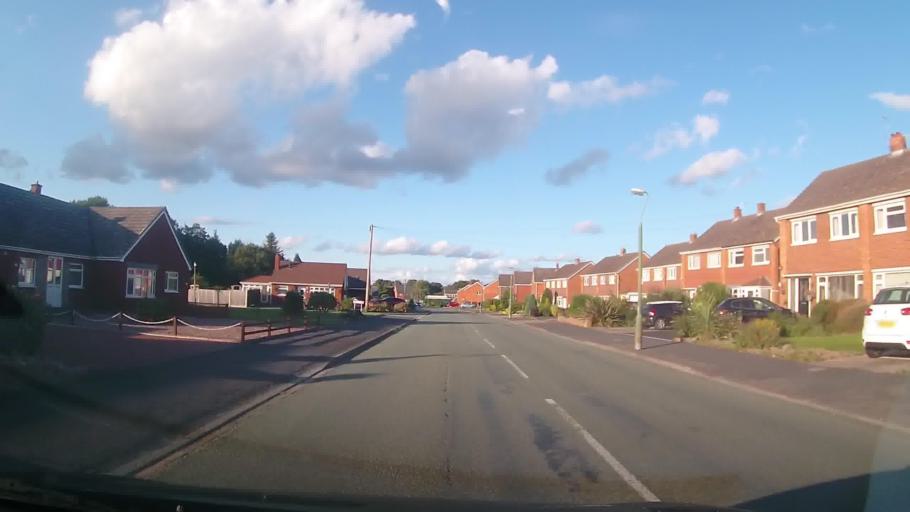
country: GB
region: England
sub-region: Shropshire
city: Shrewsbury
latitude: 52.6901
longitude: -2.7347
